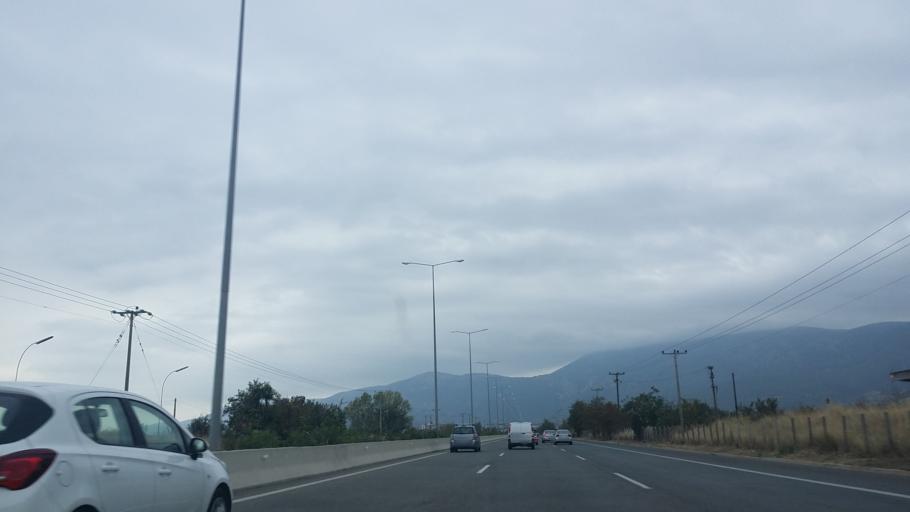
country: GR
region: Attica
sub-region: Nomarchia Anatolikis Attikis
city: Avlonas
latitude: 38.2799
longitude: 23.6861
